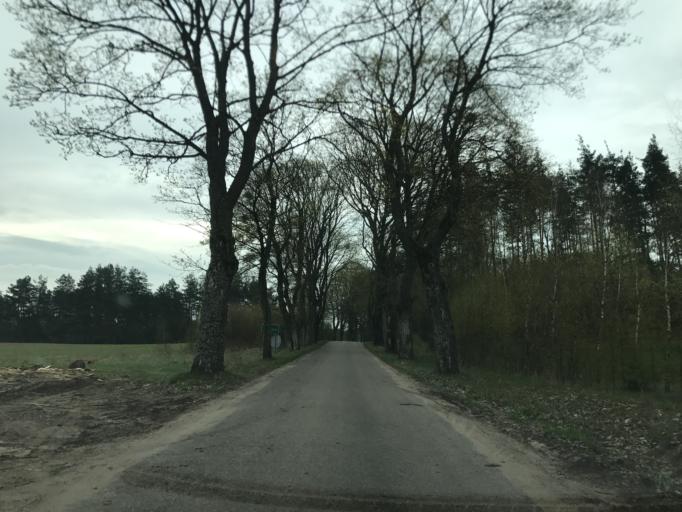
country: PL
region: Warmian-Masurian Voivodeship
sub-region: Powiat olsztynski
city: Olsztynek
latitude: 53.6151
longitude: 20.2492
